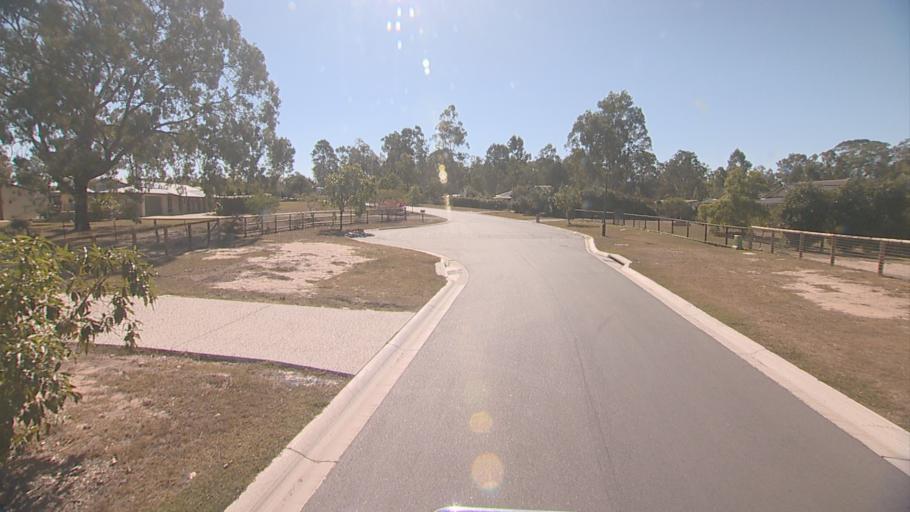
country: AU
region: Queensland
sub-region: Logan
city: Cedar Vale
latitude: -27.8614
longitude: 153.0464
